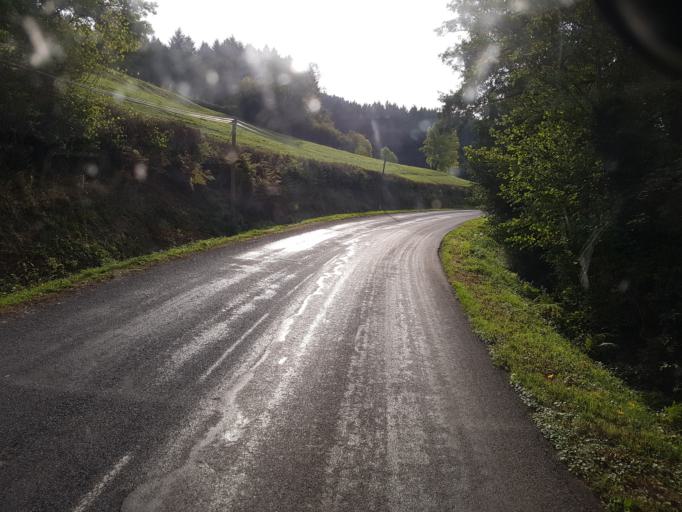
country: FR
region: Bourgogne
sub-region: Departement de Saone-et-Loire
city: Chauffailles
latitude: 46.2277
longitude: 4.4231
